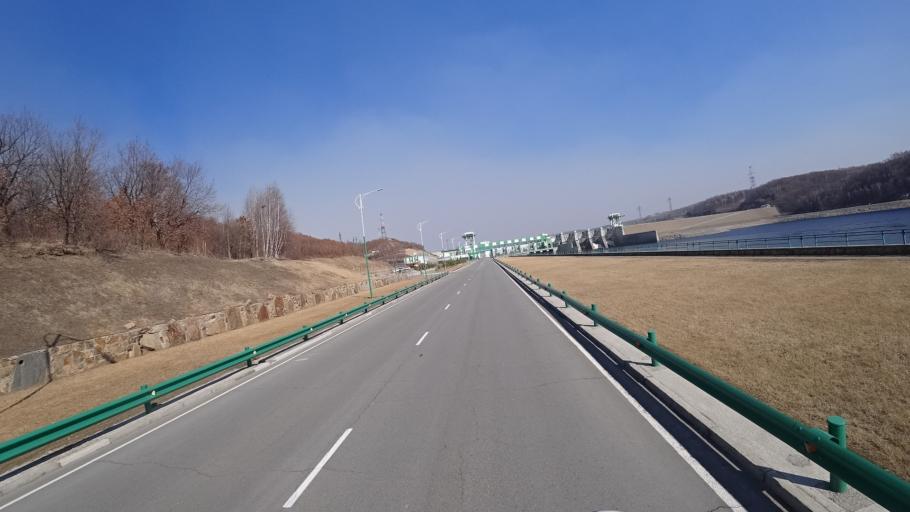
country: RU
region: Amur
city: Novobureyskiy
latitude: 49.7901
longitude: 129.9689
